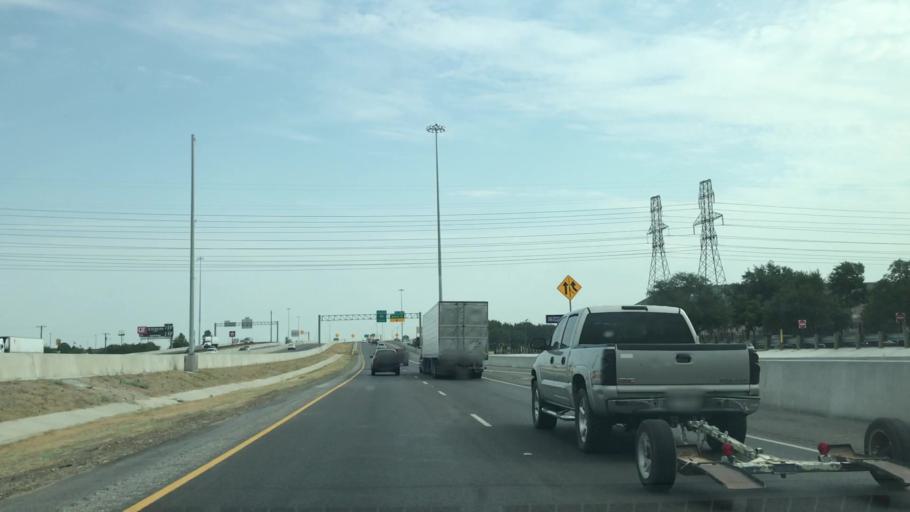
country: US
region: Texas
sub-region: Tarrant County
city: Blue Mound
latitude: 32.8194
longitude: -97.3127
